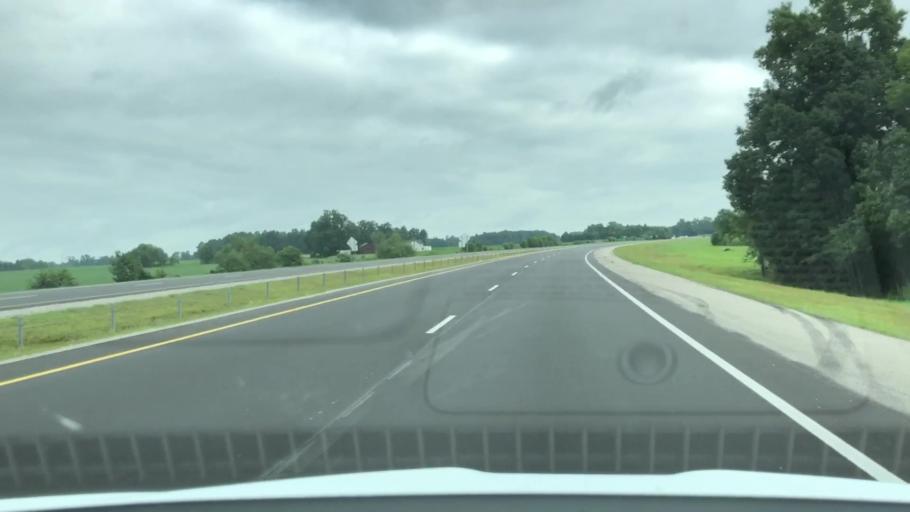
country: US
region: North Carolina
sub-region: Wayne County
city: Fremont
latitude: 35.5880
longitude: -77.9879
